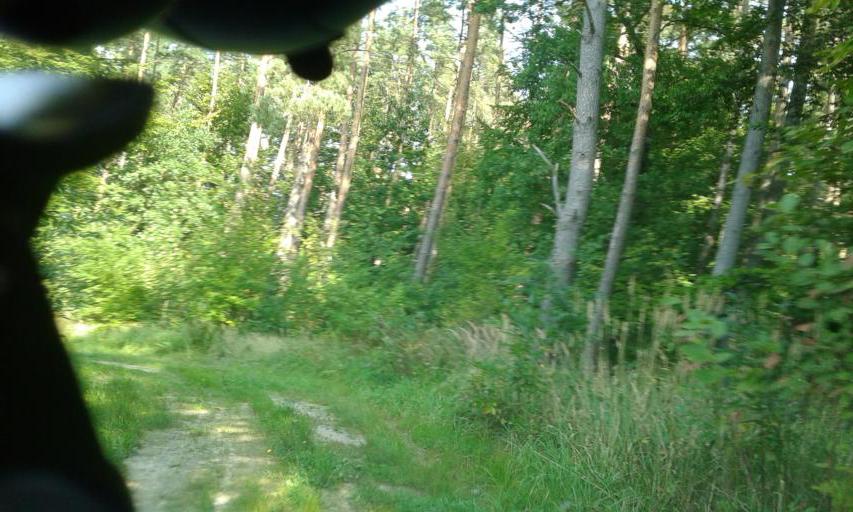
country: PL
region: West Pomeranian Voivodeship
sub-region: Powiat choszczenski
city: Krzecin
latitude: 53.0855
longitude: 15.4599
